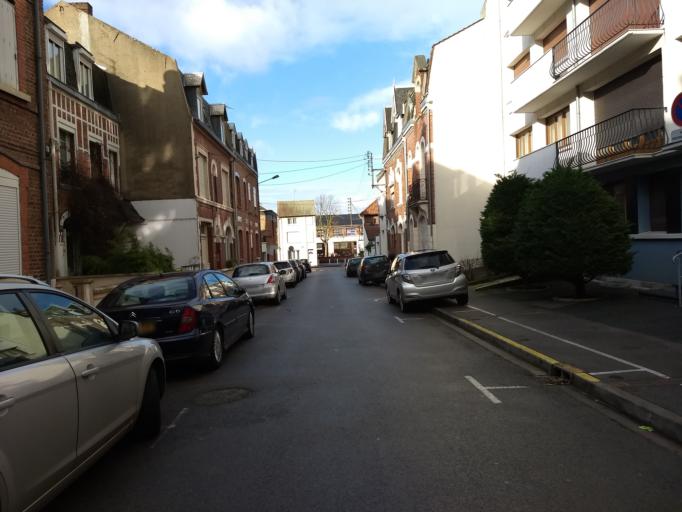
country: FR
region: Nord-Pas-de-Calais
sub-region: Departement du Pas-de-Calais
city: Arras
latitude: 50.2828
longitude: 2.7859
